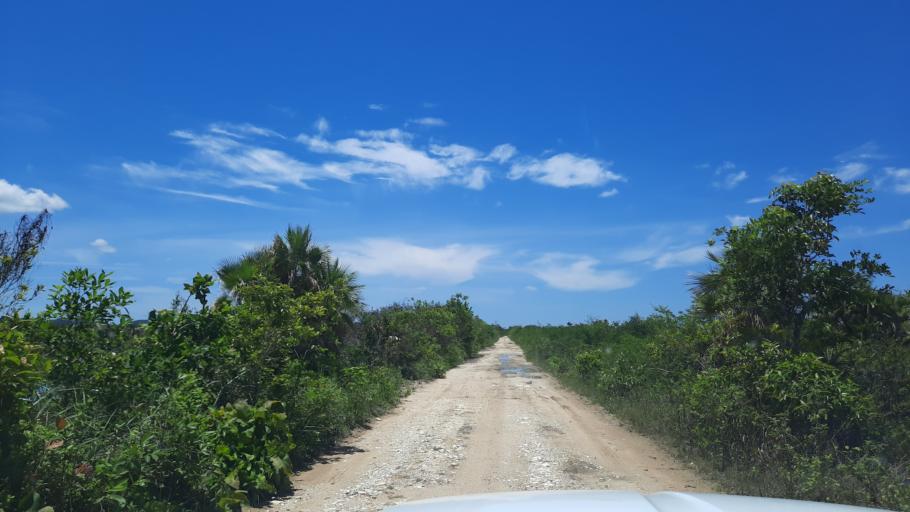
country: BZ
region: Cayo
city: Belmopan
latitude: 17.3828
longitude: -88.4932
